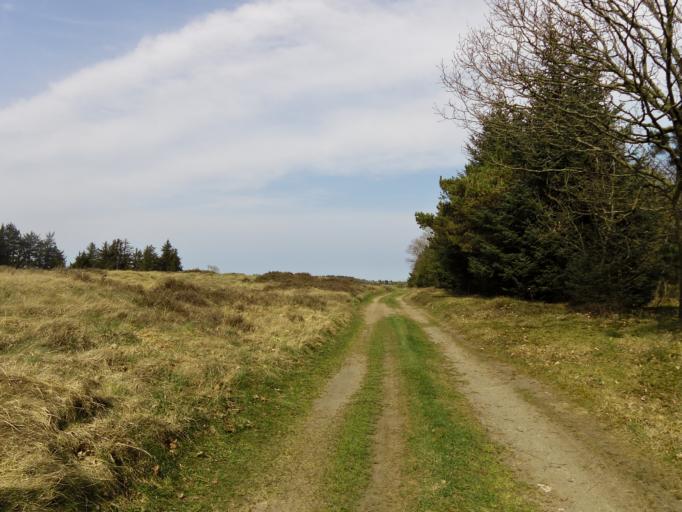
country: DK
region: South Denmark
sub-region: Esbjerg Kommune
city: Ribe
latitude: 55.3198
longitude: 8.8603
